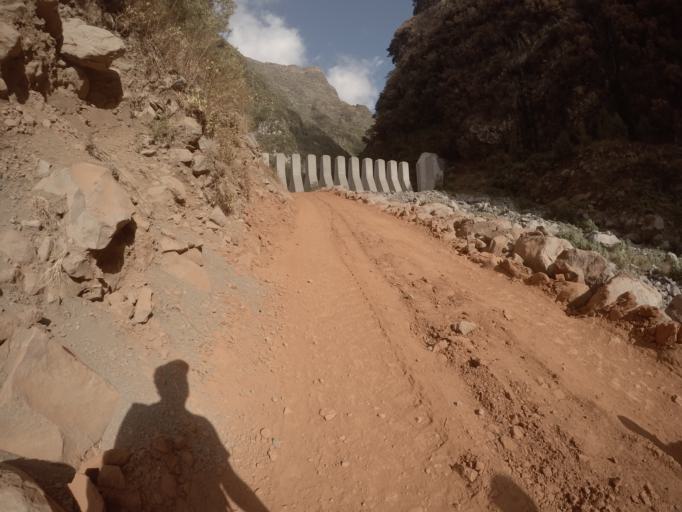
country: PT
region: Madeira
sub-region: Funchal
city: Nossa Senhora do Monte
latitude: 32.6965
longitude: -16.9185
